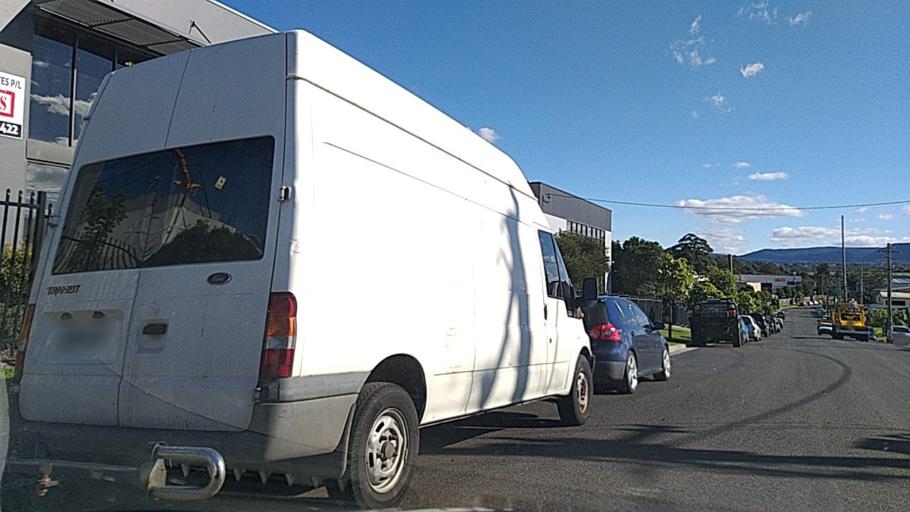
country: AU
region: New South Wales
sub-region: Wollongong
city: Berkeley
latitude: -34.4644
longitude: 150.8581
